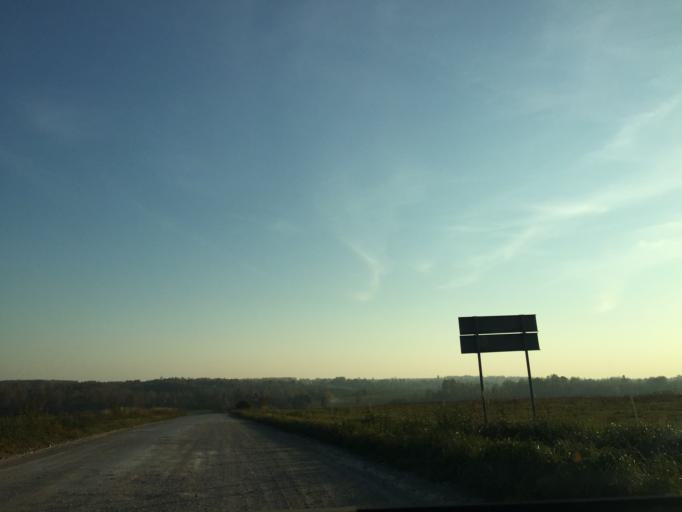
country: LV
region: Vainode
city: Vainode
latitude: 56.5679
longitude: 21.8480
